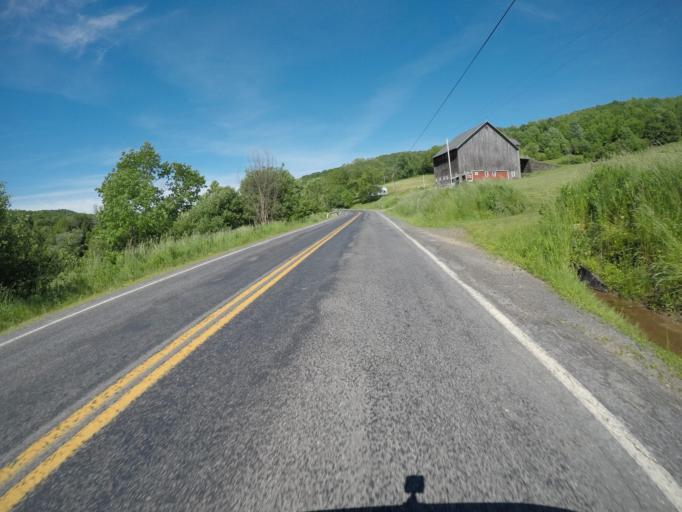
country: US
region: New York
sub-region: Delaware County
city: Delhi
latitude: 42.2123
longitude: -74.9356
